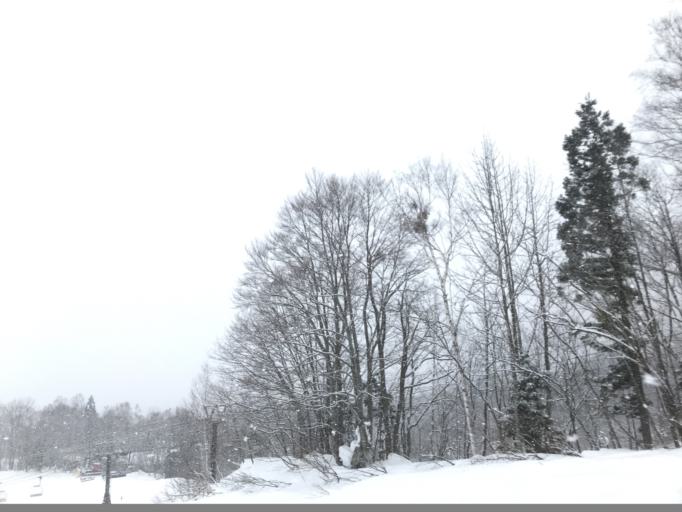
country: JP
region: Nagano
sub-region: Kitaazumi Gun
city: Hakuba
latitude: 36.7532
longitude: 137.8483
